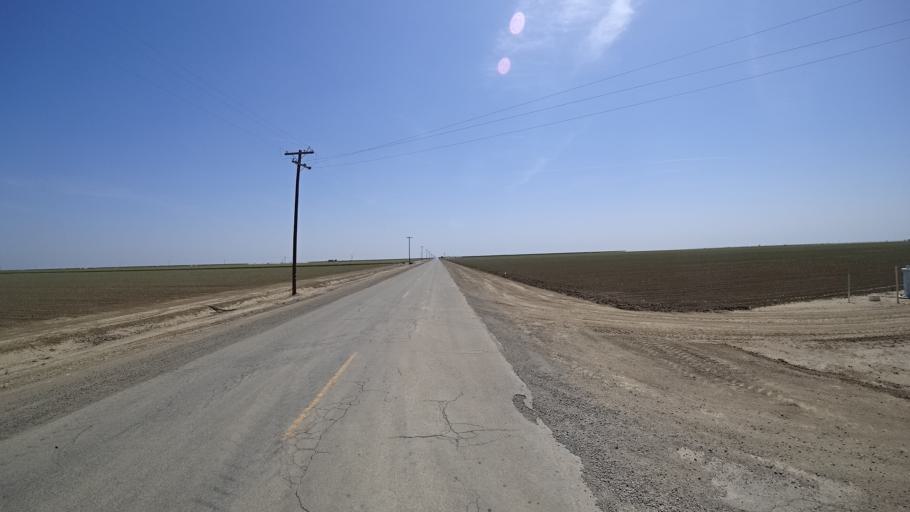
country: US
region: California
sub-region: Kings County
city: Kettleman City
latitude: 36.1377
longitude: -119.9837
